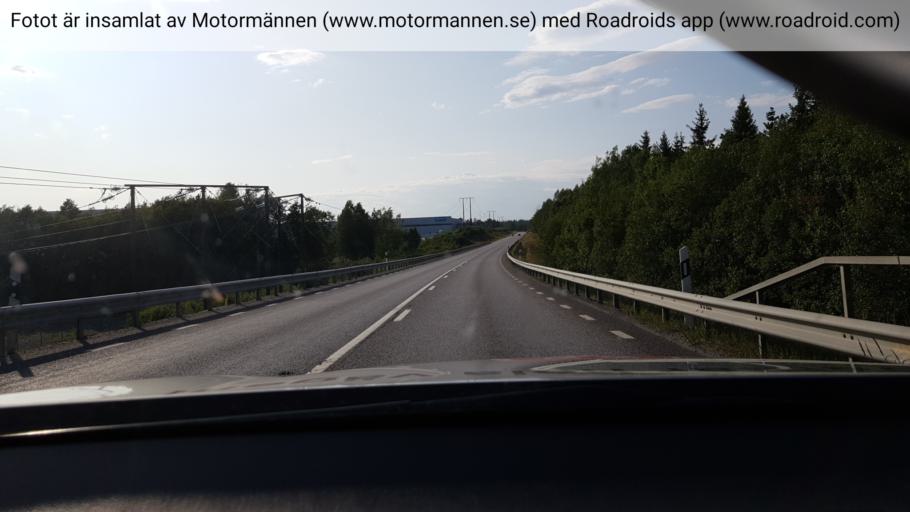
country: SE
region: Stockholm
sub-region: Haninge Kommun
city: Jordbro
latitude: 59.1552
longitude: 18.1249
